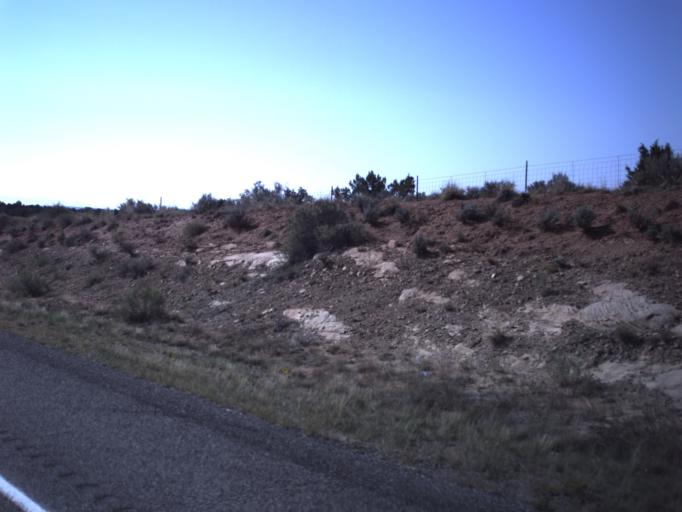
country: US
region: Utah
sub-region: San Juan County
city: Blanding
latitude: 37.4855
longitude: -109.4743
